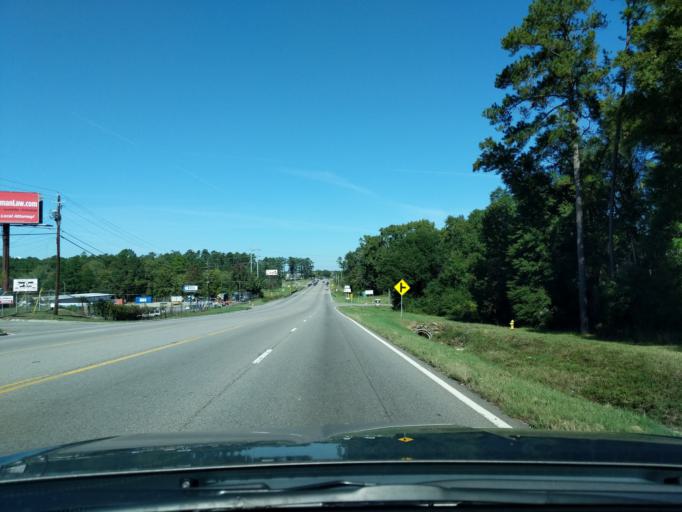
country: US
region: Georgia
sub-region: Richmond County
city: Augusta
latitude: 33.3818
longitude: -82.0026
